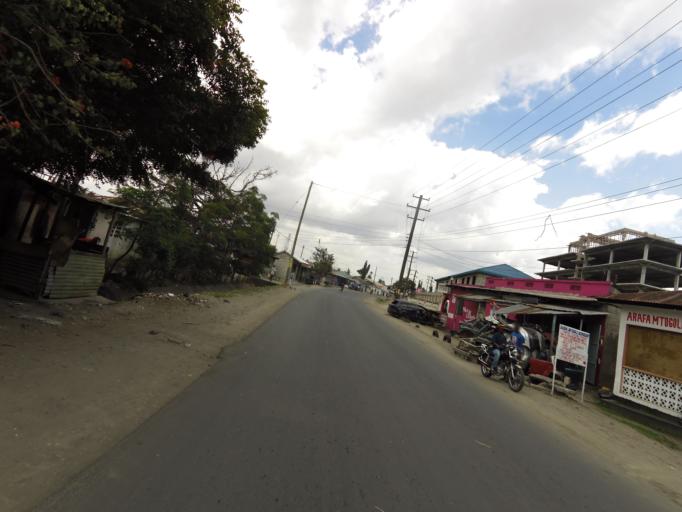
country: TZ
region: Dar es Salaam
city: Magomeni
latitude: -6.7917
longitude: 39.2409
